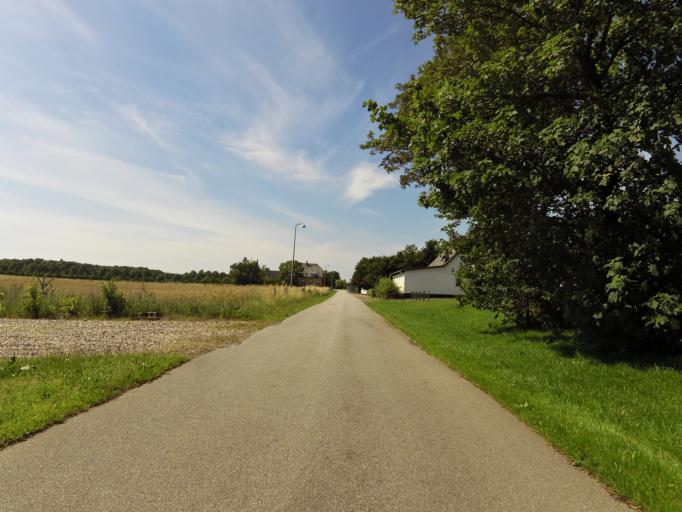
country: DK
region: South Denmark
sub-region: Esbjerg Kommune
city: Ribe
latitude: 55.2611
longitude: 8.8957
